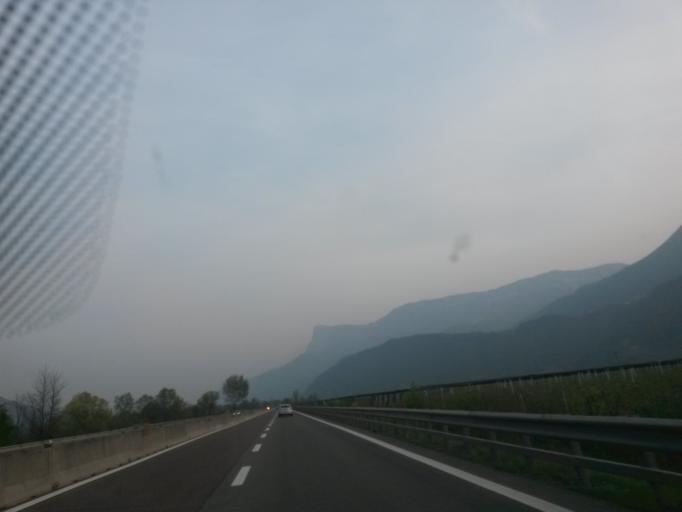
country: IT
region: Trentino-Alto Adige
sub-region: Bolzano
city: Postal
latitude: 46.6030
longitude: 11.1837
